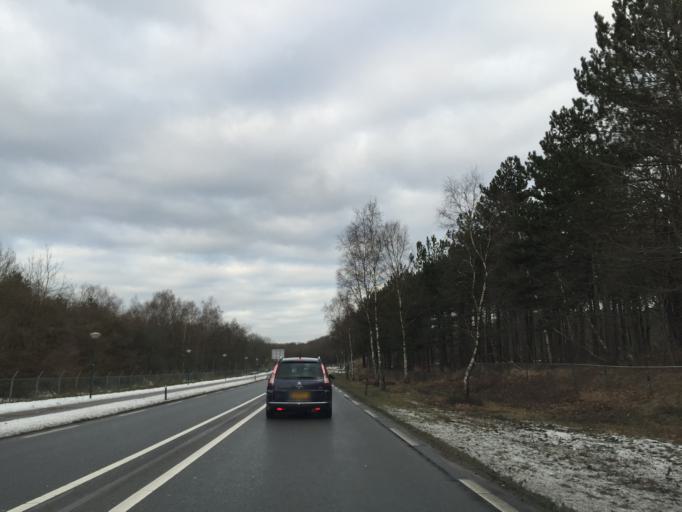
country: NL
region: Utrecht
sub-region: Gemeente Soest
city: Soest
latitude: 52.1290
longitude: 5.2996
